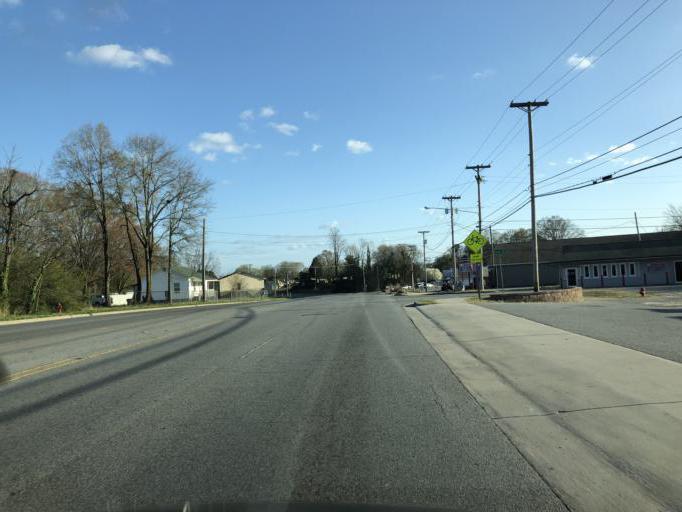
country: US
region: North Carolina
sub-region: Gaston County
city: Gastonia
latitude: 35.2697
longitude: -81.2225
